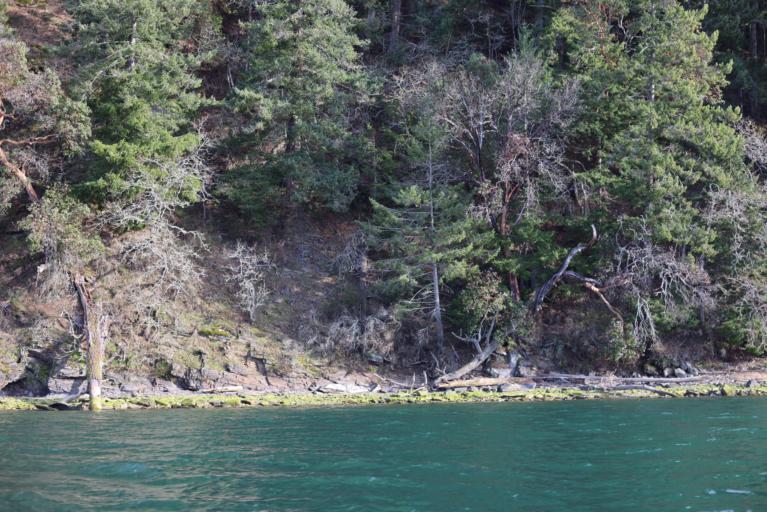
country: CA
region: British Columbia
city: Duncan
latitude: 48.7573
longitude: -123.6096
